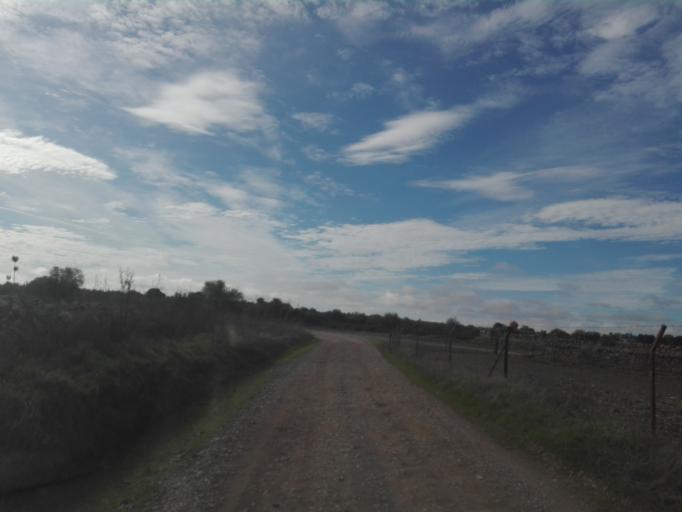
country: ES
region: Extremadura
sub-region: Provincia de Badajoz
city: Villagarcia de la Torre
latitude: 38.3020
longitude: -6.0865
